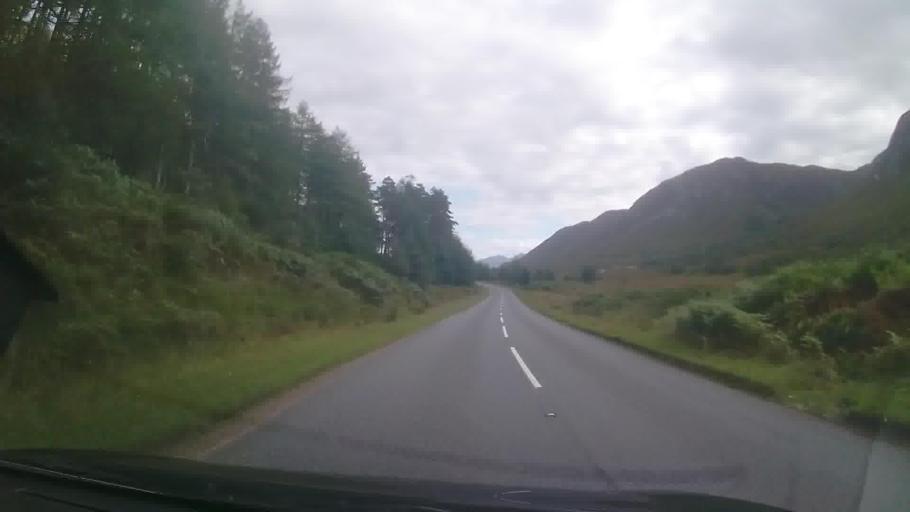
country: GB
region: Scotland
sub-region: Argyll and Bute
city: Oban
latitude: 56.6884
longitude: -5.4655
